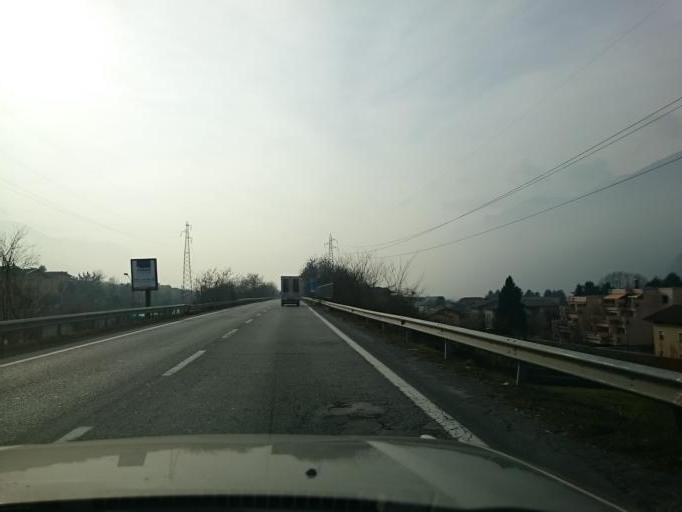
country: IT
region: Lombardy
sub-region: Provincia di Brescia
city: Darfo
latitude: 45.8770
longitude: 10.1858
